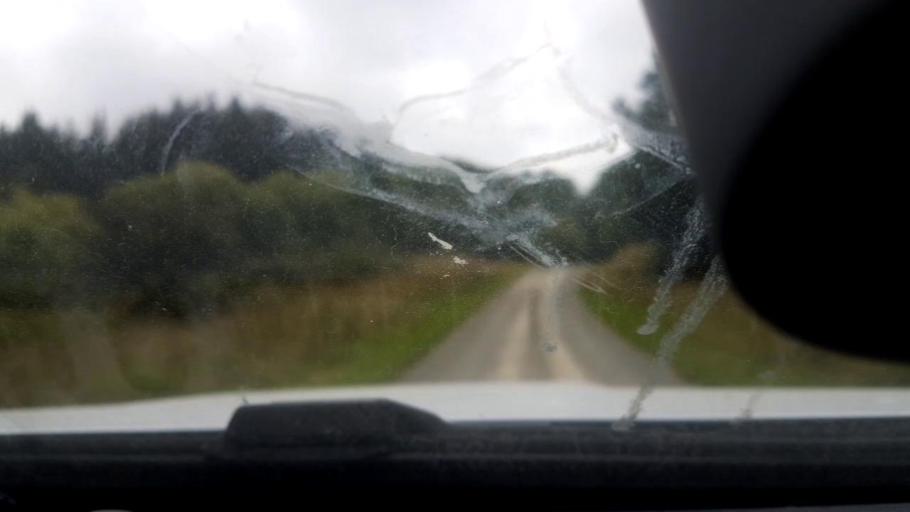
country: NZ
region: Canterbury
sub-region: Timaru District
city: Pleasant Point
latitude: -44.1299
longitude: 171.0863
